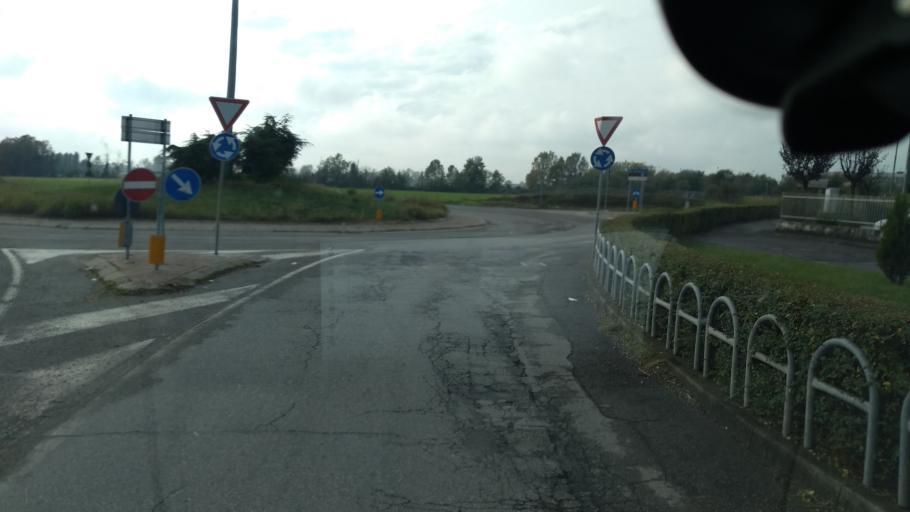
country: IT
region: Lombardy
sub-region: Provincia di Bergamo
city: Brignano Gera d'Adda
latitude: 45.5367
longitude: 9.6392
